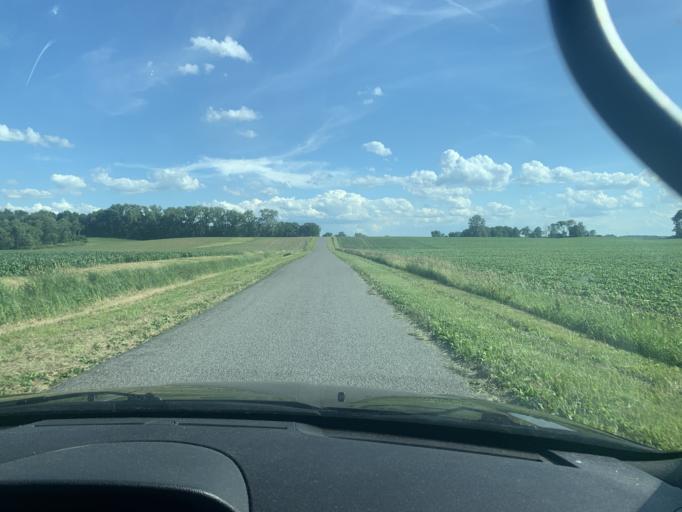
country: US
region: Ohio
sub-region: Logan County
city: De Graff
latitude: 40.3178
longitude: -83.8739
